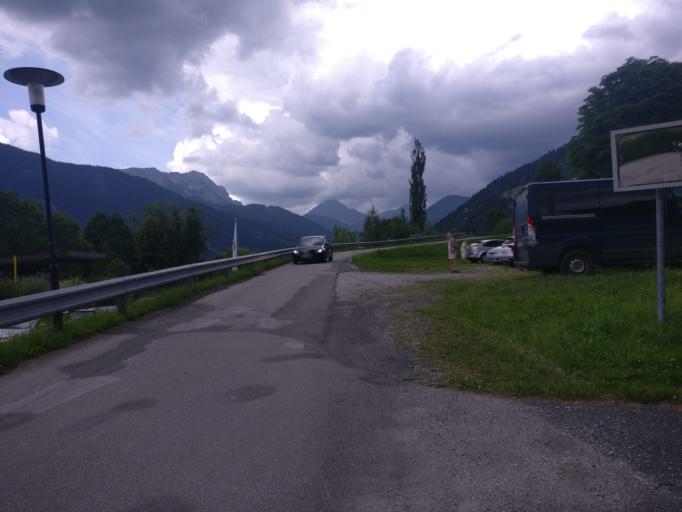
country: AT
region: Styria
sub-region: Politischer Bezirk Liezen
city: Selzthal
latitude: 47.5589
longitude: 14.3223
